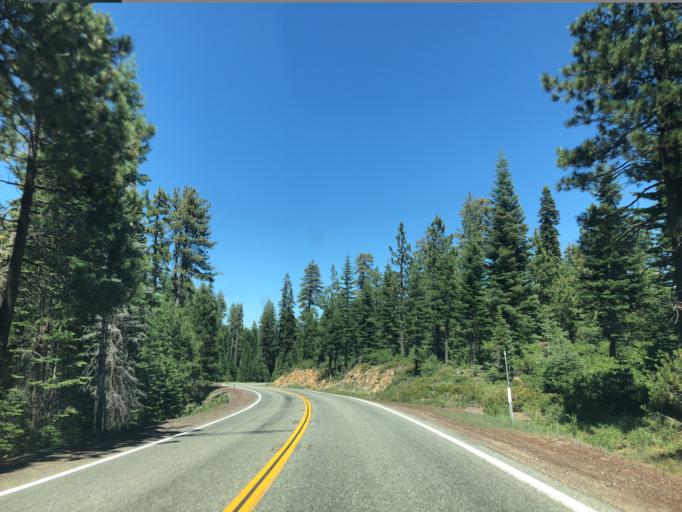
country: US
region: California
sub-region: Shasta County
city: Burney
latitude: 40.5728
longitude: -121.5712
